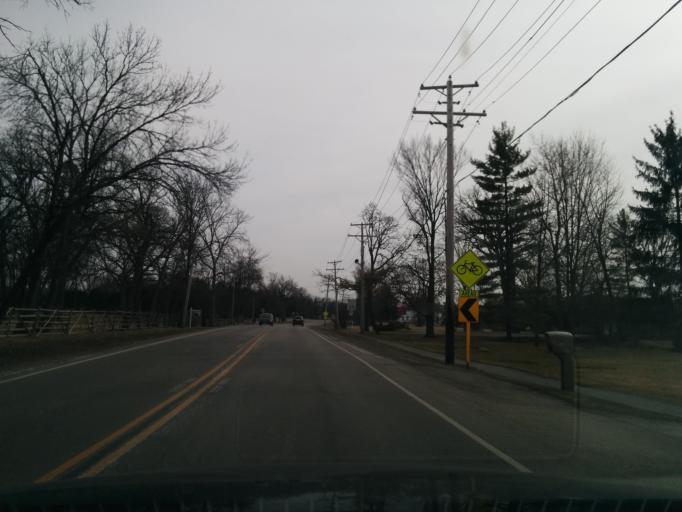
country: US
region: Illinois
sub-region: DuPage County
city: Oak Brook
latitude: 41.8274
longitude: -87.9280
